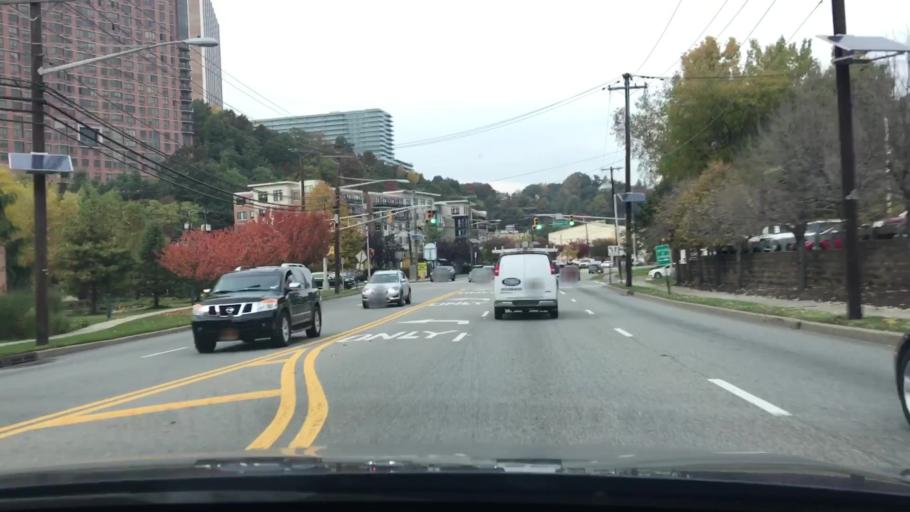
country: US
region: New Jersey
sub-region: Bergen County
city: Fairview
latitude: 40.8088
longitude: -73.9897
